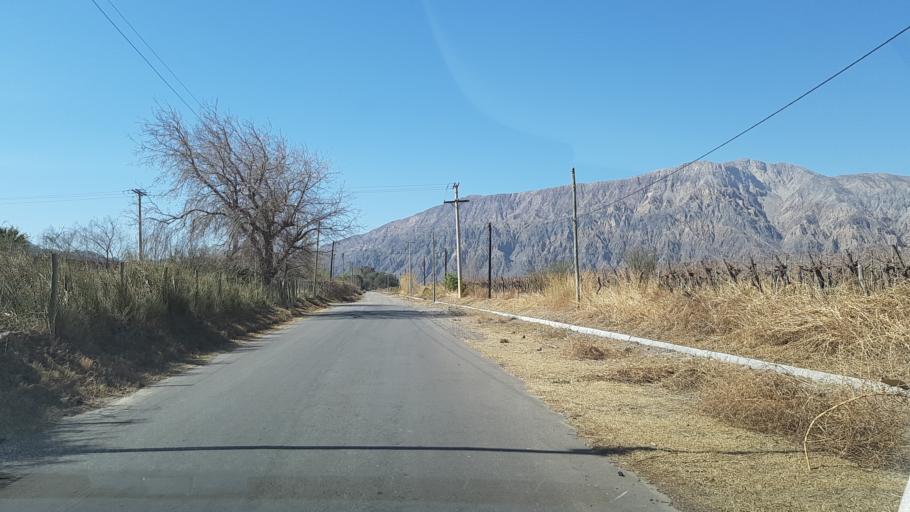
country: AR
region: San Juan
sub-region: Departamento de Zonda
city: Zonda
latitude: -31.5712
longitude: -68.7508
